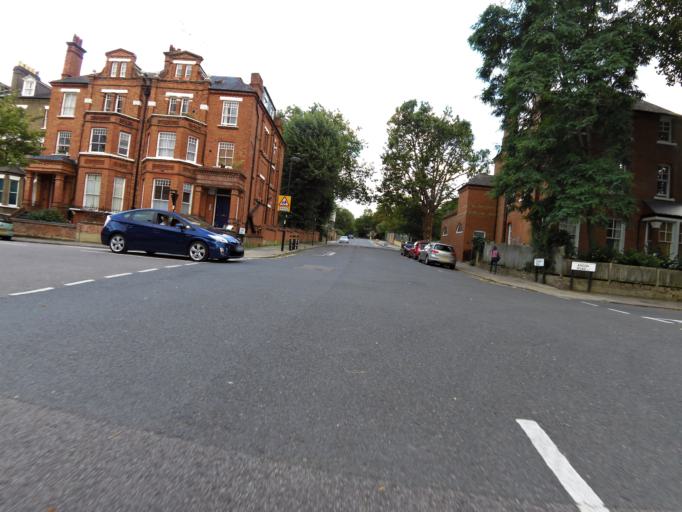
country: GB
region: England
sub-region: Greater London
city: Holloway
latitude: 51.5554
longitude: -0.1297
